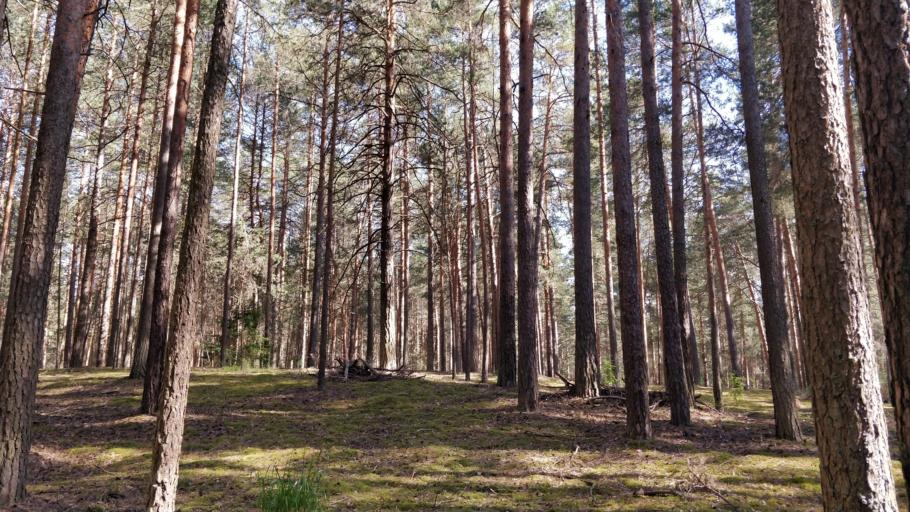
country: RU
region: Perm
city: Perm
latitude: 58.0689
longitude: 56.2880
